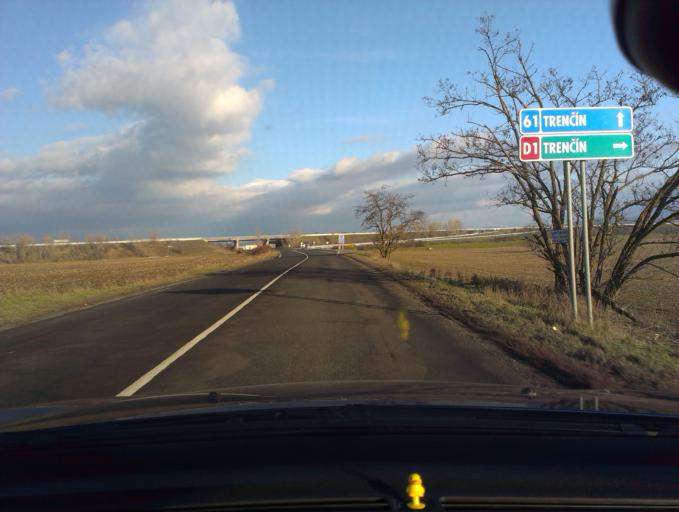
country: SK
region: Trnavsky
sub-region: Okres Trnava
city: Piestany
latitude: 48.6456
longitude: 17.8385
